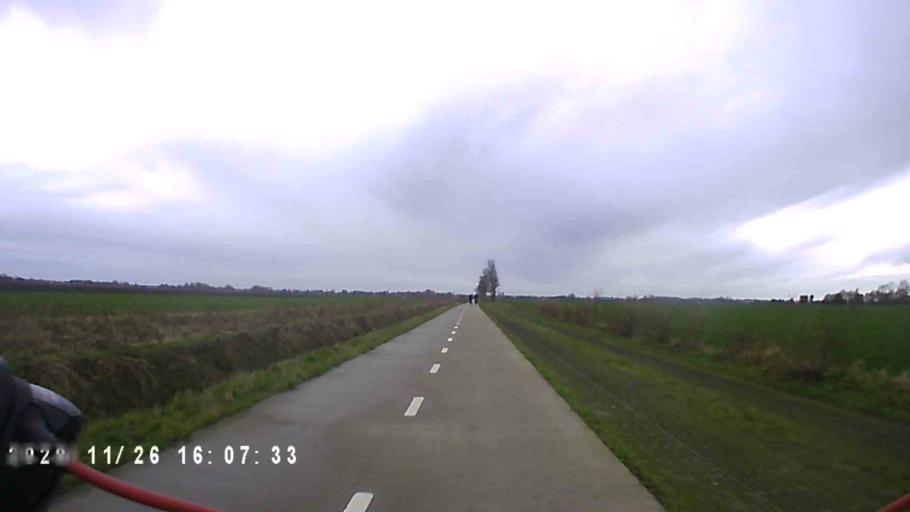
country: NL
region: Groningen
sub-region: Gemeente Bedum
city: Bedum
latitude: 53.2613
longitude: 6.6666
